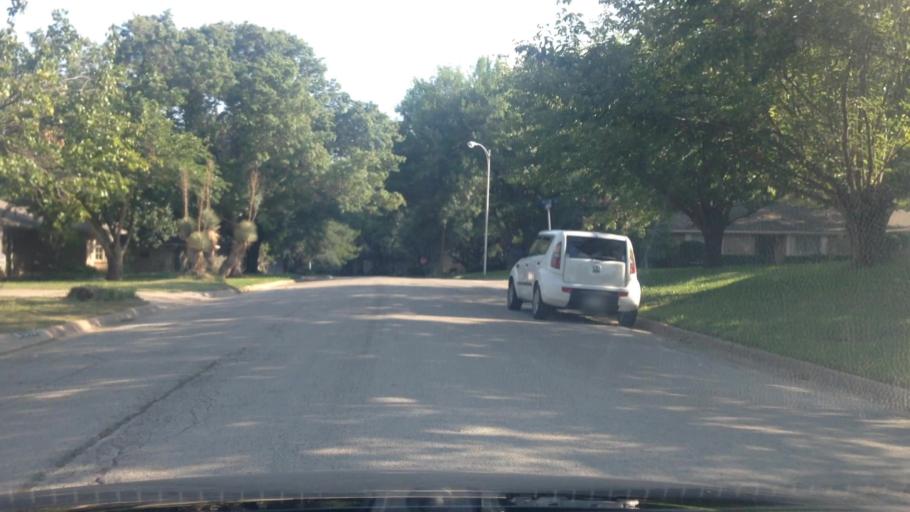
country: US
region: Texas
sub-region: Tarrant County
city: Edgecliff Village
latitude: 32.6564
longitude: -97.3388
